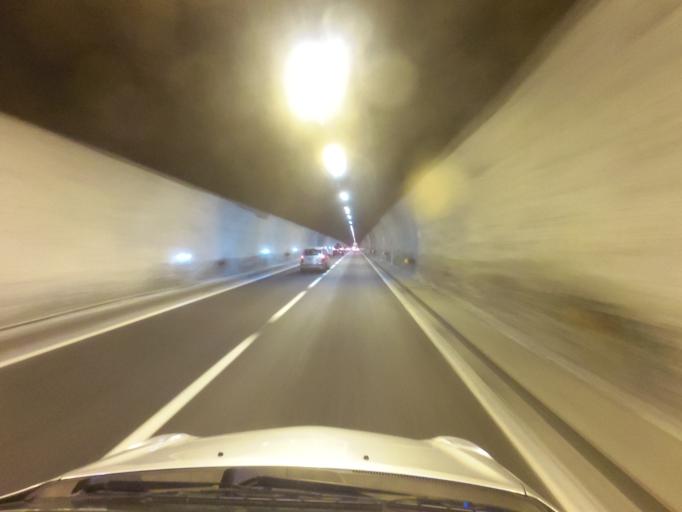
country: IT
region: Tuscany
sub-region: Province of Florence
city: Cavallina
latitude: 43.9459
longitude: 11.2145
